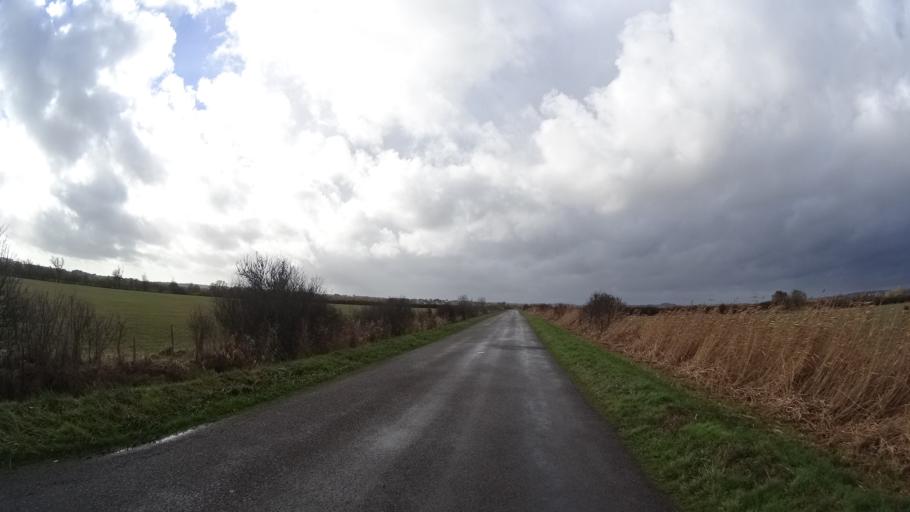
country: FR
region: Brittany
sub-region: Departement du Morbihan
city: Rieux
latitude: 47.5803
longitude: -2.0871
